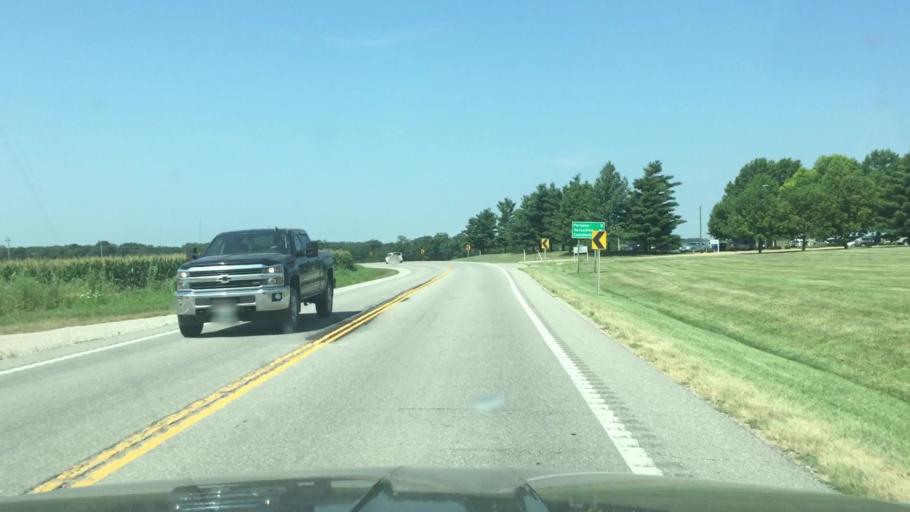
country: US
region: Missouri
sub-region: Moniteau County
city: Tipton
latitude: 38.6421
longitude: -92.7865
